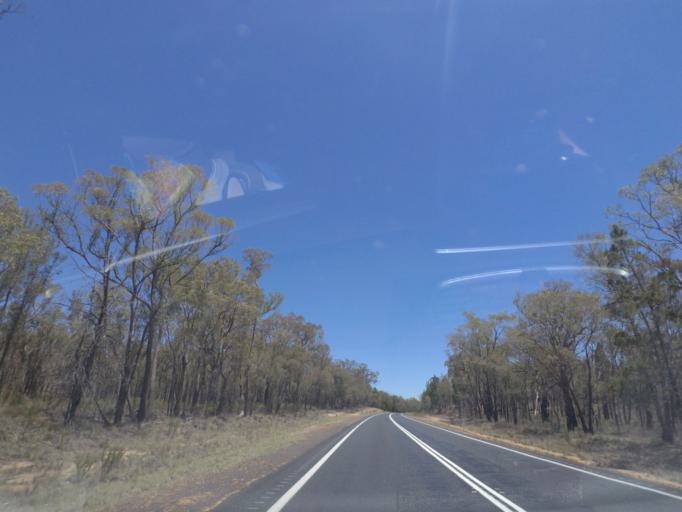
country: AU
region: New South Wales
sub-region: Warrumbungle Shire
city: Coonabarabran
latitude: -31.1922
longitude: 149.3531
